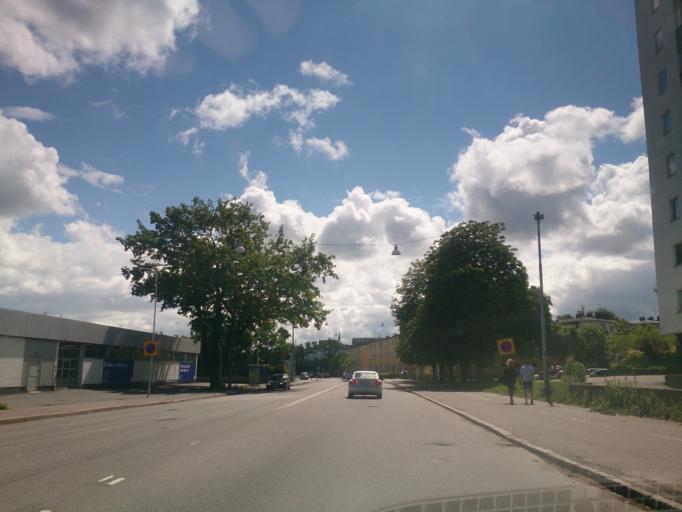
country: SE
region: OEstergoetland
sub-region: Norrkopings Kommun
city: Norrkoping
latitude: 58.6018
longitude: 16.1665
